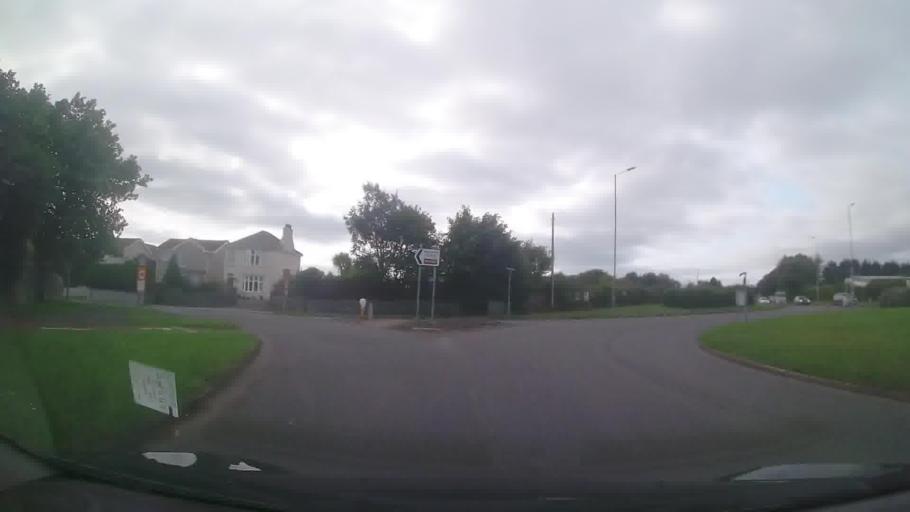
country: GB
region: Wales
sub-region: Pembrokeshire
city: Neyland
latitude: 51.7173
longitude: -4.9550
